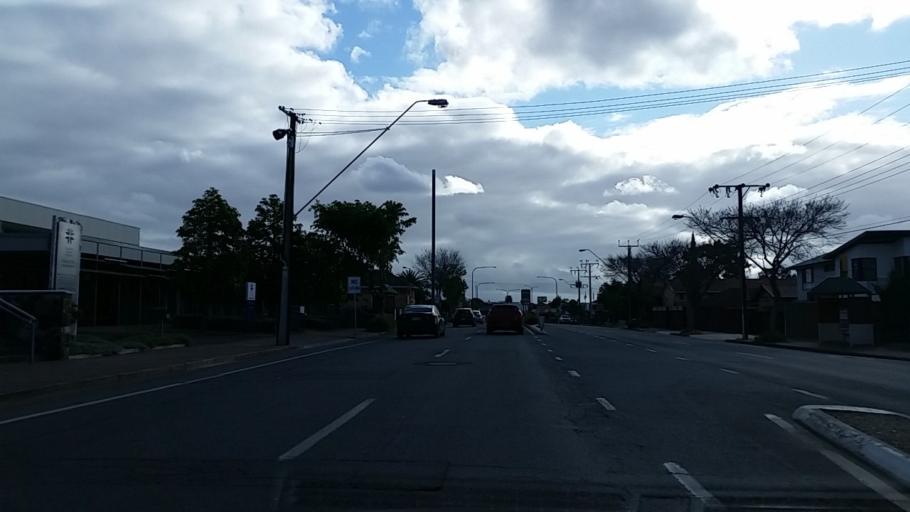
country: AU
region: South Australia
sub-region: Campbelltown
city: Hectorville
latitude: -34.8894
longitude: 138.6592
